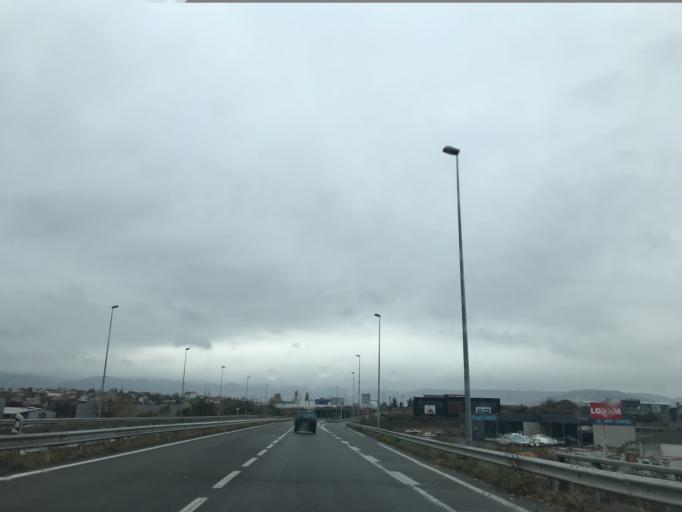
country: FR
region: Auvergne
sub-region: Departement du Puy-de-Dome
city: Aubiere
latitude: 45.7763
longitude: 3.1353
